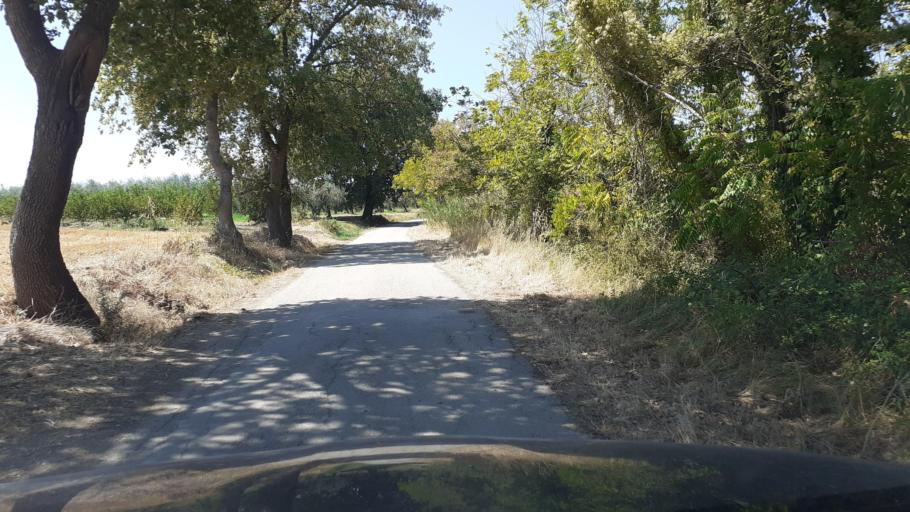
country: IT
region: Abruzzo
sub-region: Provincia di Chieti
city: Santa Maria Imbaro
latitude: 42.2099
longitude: 14.4691
